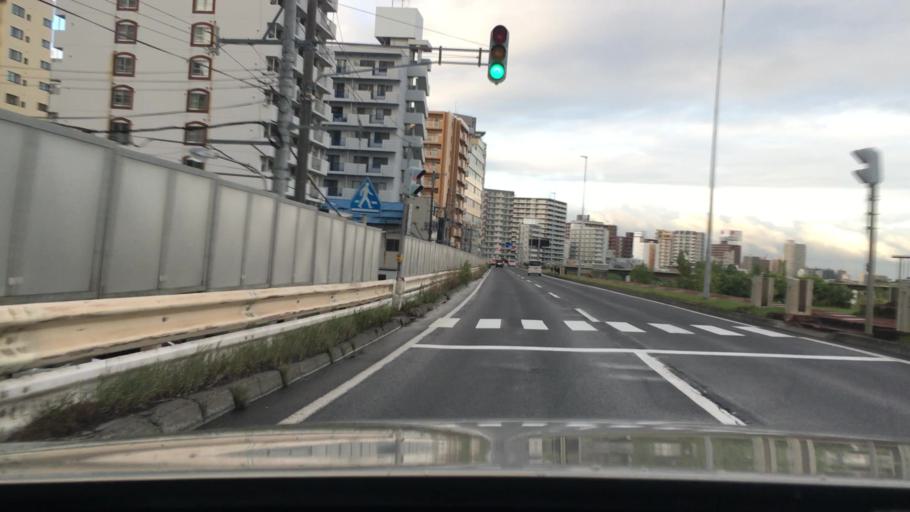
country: JP
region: Hokkaido
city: Sapporo
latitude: 43.0499
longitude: 141.3590
